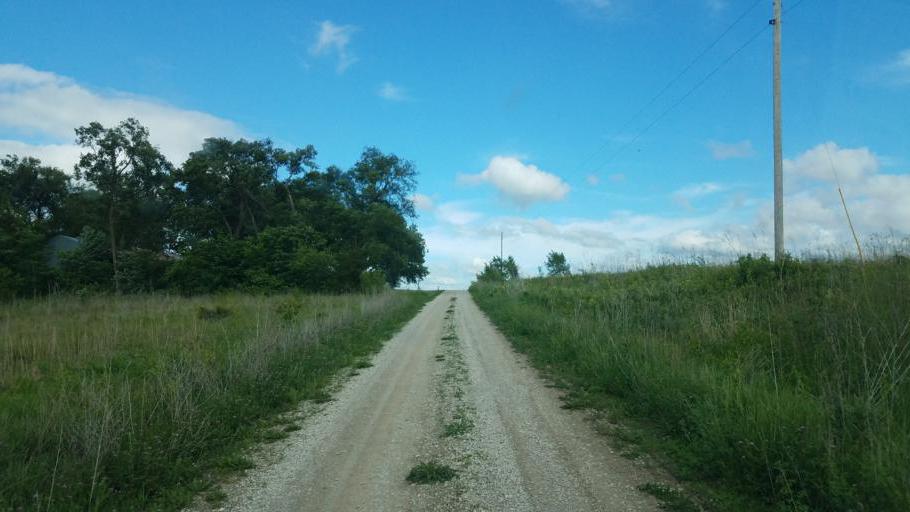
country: US
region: Missouri
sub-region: Mercer County
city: Princeton
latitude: 40.2601
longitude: -93.7023
